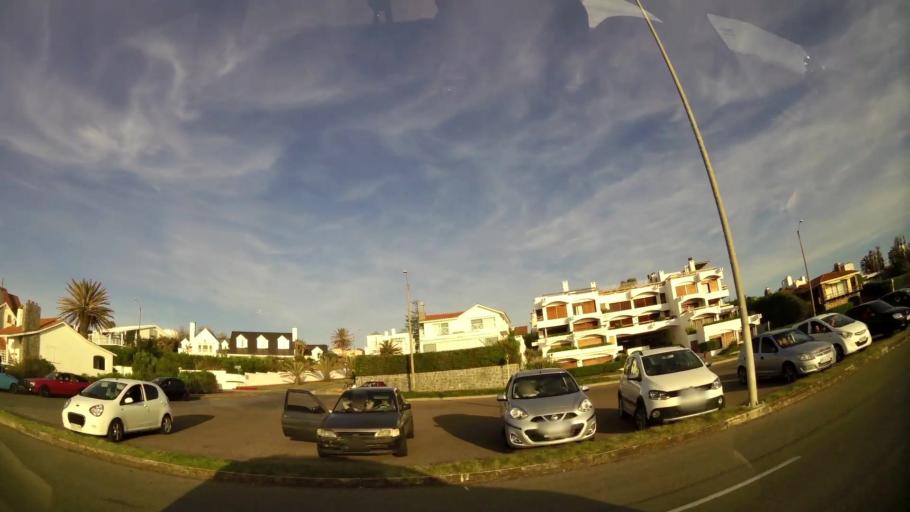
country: UY
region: Maldonado
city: Punta del Este
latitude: -34.9686
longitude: -54.9543
